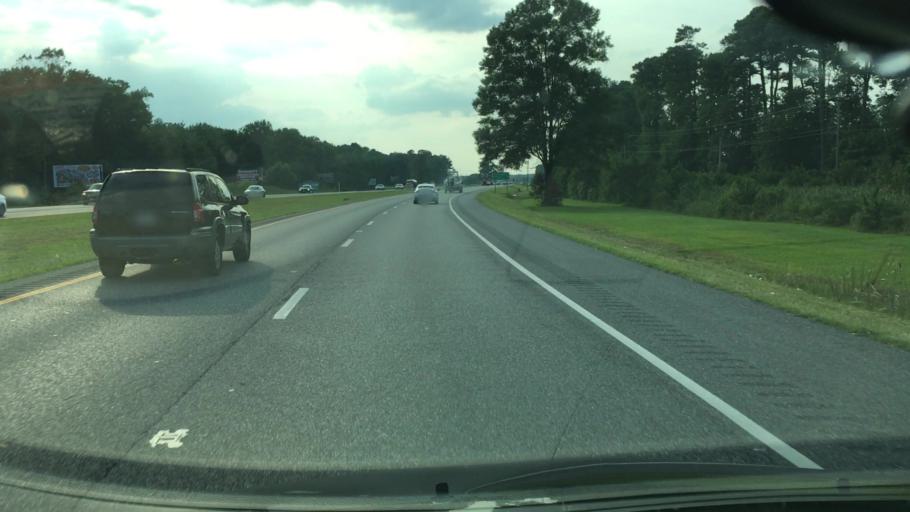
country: US
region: Maryland
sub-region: Worcester County
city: West Ocean City
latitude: 38.3382
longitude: -75.1490
